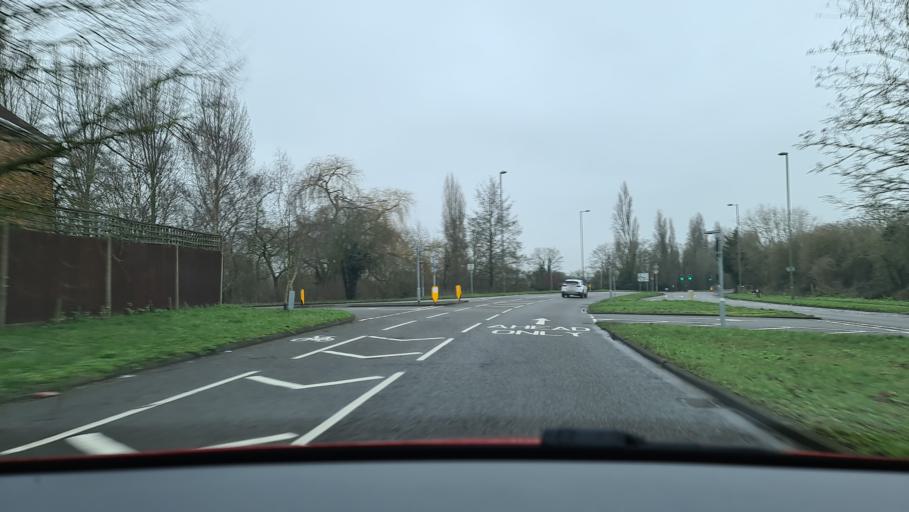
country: GB
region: England
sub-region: Surrey
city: Shepperton
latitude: 51.3994
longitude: -0.4334
